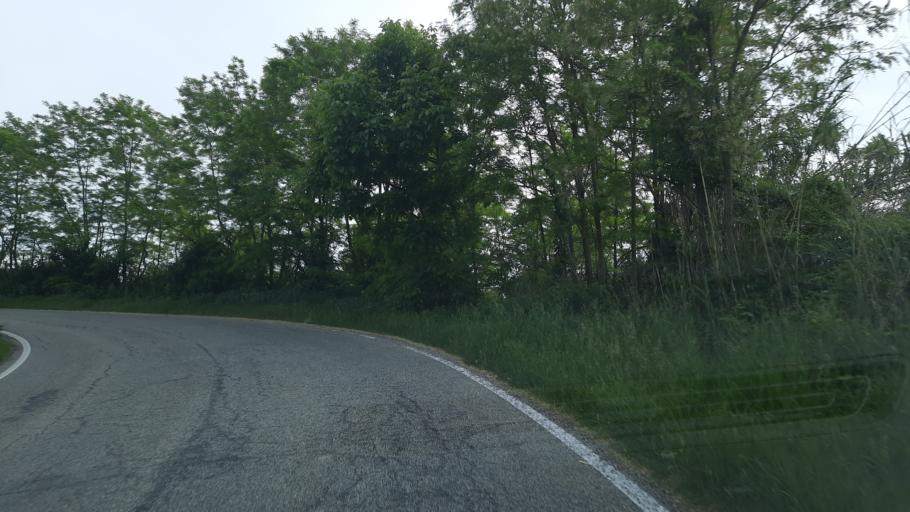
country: IT
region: Piedmont
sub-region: Provincia di Alessandria
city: Coniolo Bricco
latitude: 45.1387
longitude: 8.3565
